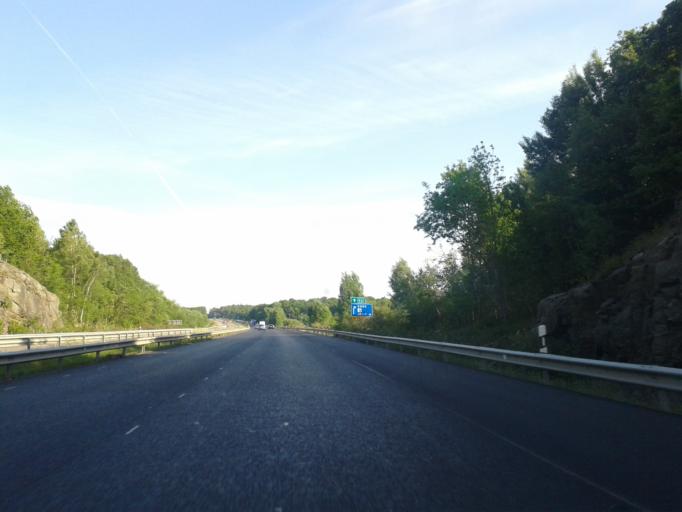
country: SE
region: Vaestra Goetaland
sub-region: Kungalvs Kommun
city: Kode
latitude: 57.9324
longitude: 11.8722
